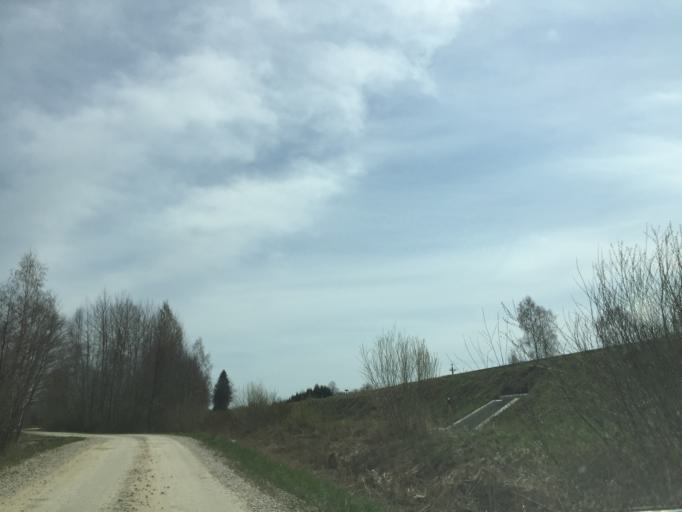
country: LV
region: Ludzas Rajons
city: Ludza
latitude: 56.5355
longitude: 27.5298
